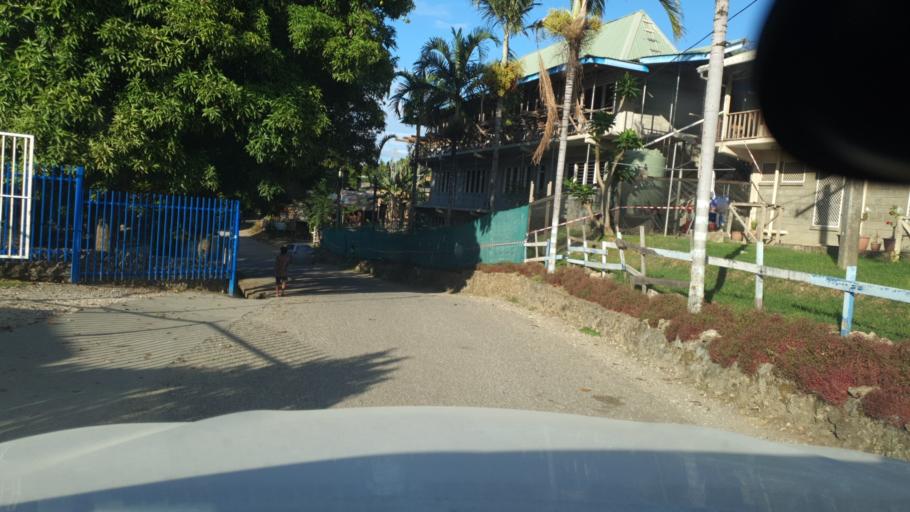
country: SB
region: Guadalcanal
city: Honiara
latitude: -9.4355
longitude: 159.9771
